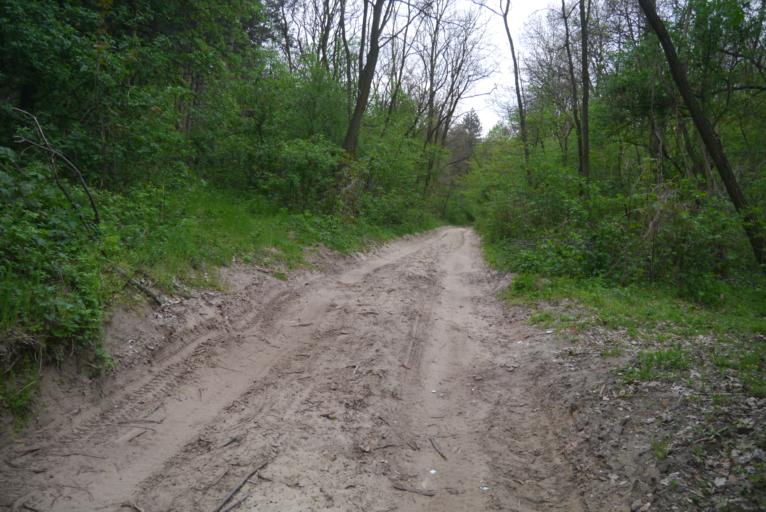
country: HU
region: Komarom-Esztergom
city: Piliscsev
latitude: 47.6663
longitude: 18.8284
